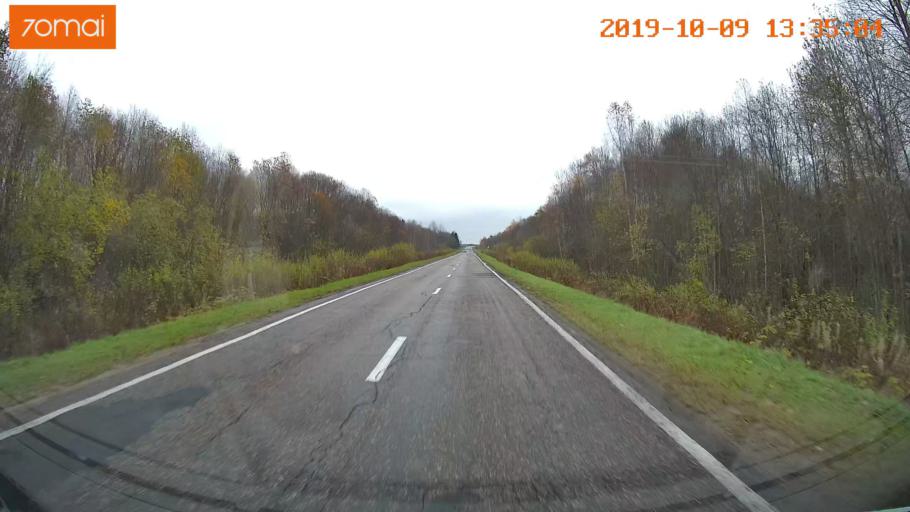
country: RU
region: Jaroslavl
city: Lyubim
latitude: 58.3338
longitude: 41.0710
